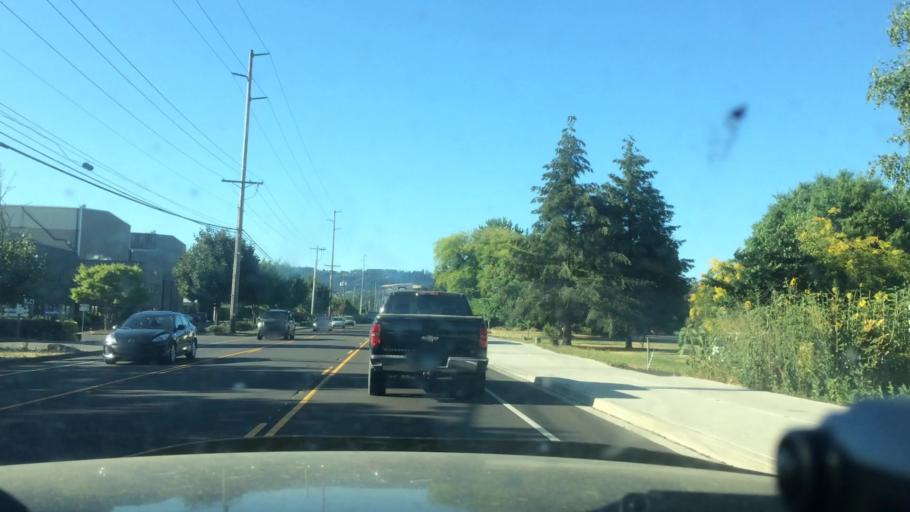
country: US
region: Oregon
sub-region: Yamhill County
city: Newberg
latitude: 45.2945
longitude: -122.9470
